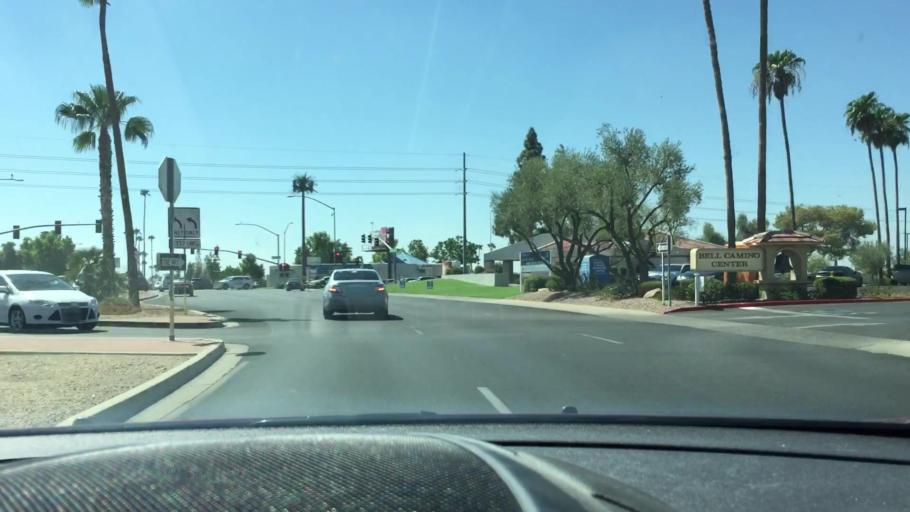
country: US
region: Arizona
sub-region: Maricopa County
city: El Mirage
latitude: 33.6391
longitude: -112.2898
